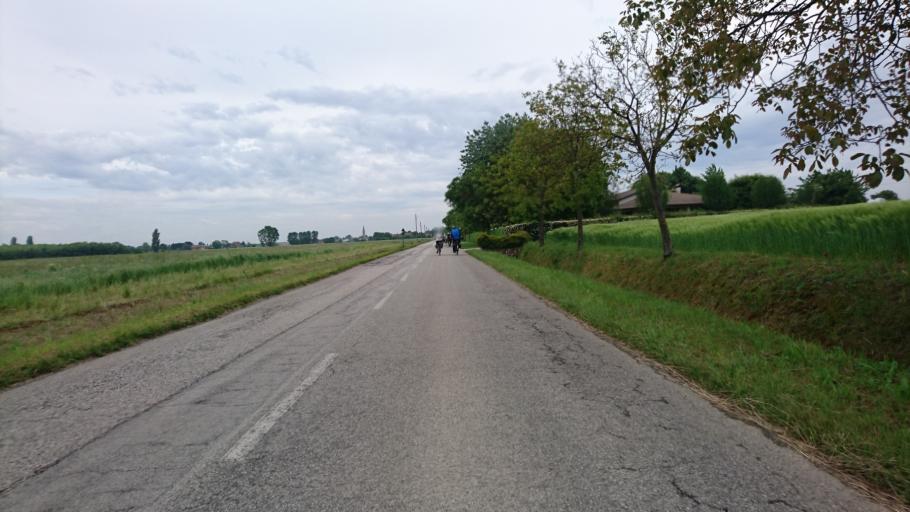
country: IT
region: Veneto
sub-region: Provincia di Padova
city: Cervarese Santa Croce
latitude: 45.4156
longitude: 11.6705
